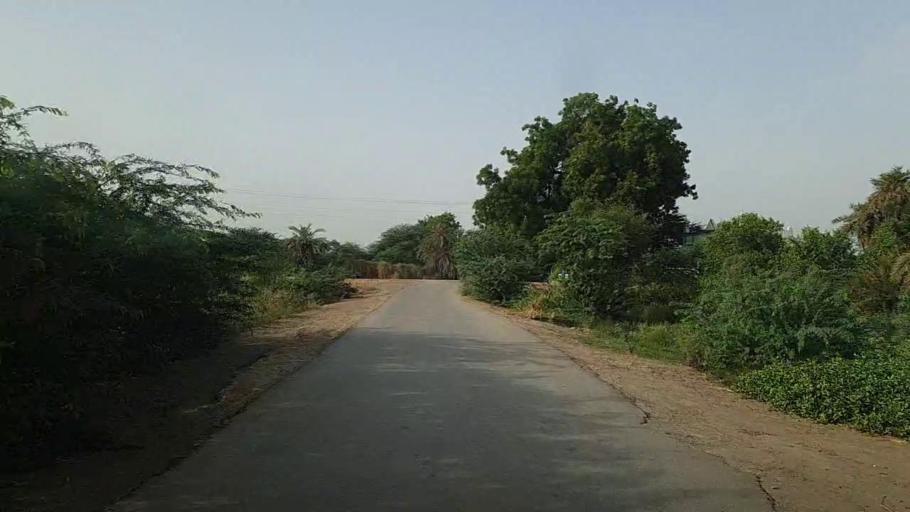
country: PK
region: Sindh
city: Mehar
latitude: 27.1315
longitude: 67.7910
